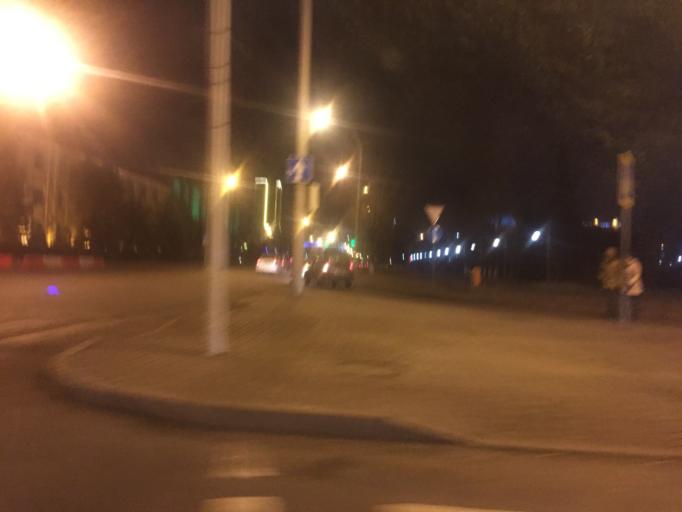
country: KZ
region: Astana Qalasy
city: Astana
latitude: 51.1667
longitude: 71.4139
